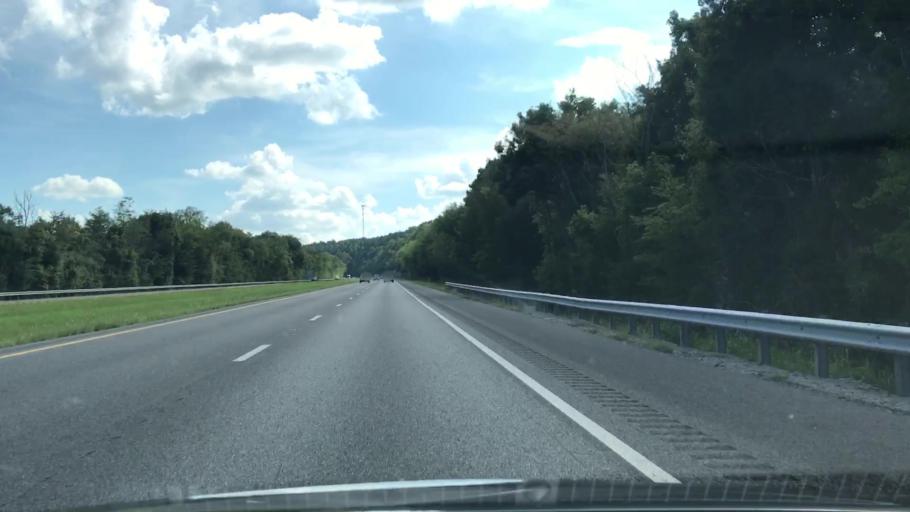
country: US
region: Tennessee
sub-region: Marshall County
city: Cornersville
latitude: 35.4119
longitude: -86.8781
